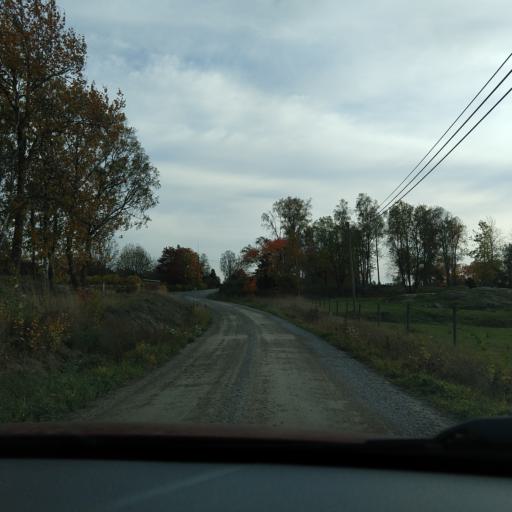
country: SE
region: Stockholm
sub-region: Vallentuna Kommun
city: Vallentuna
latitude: 59.5268
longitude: 18.0137
